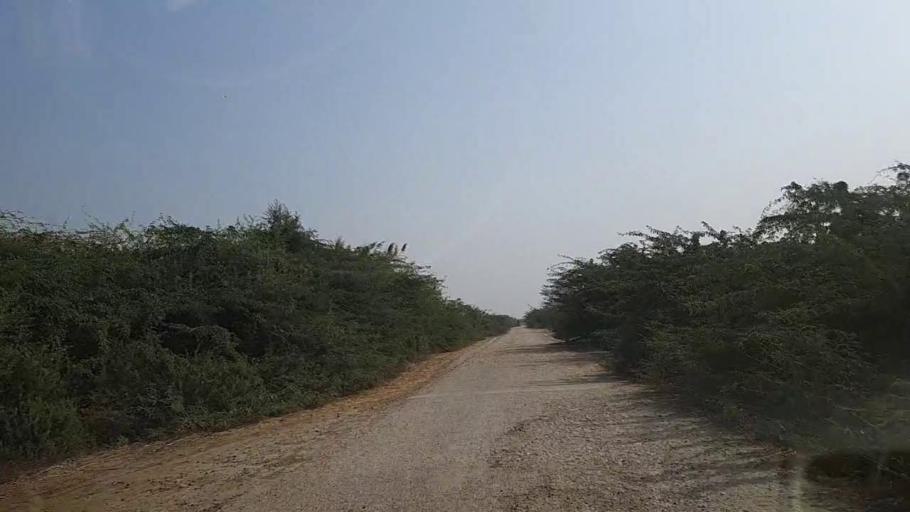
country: PK
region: Sindh
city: Keti Bandar
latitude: 24.2504
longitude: 67.6300
